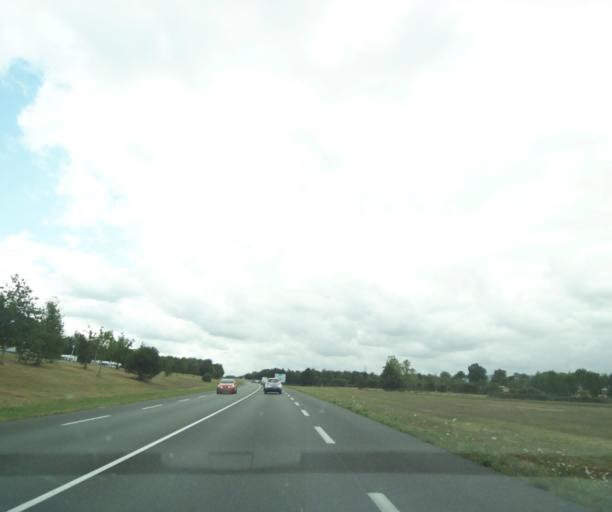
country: FR
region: Pays de la Loire
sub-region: Departement de la Vendee
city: Les Clouzeaux
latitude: 46.6517
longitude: -1.5083
